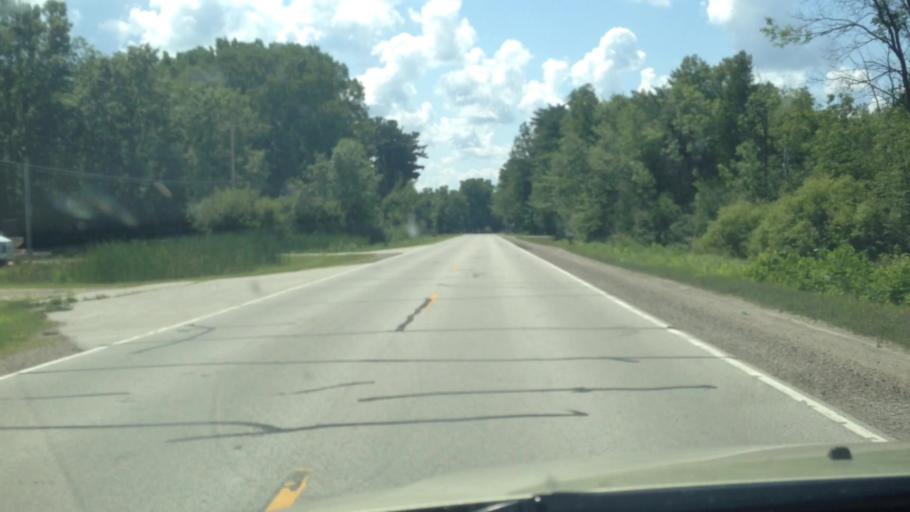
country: US
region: Wisconsin
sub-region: Brown County
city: Suamico
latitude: 44.6419
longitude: -88.0497
